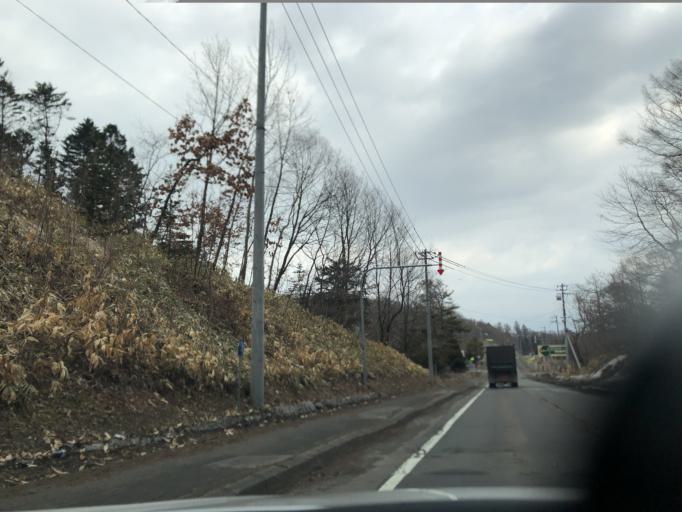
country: JP
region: Hokkaido
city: Chitose
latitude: 42.7582
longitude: 141.7954
